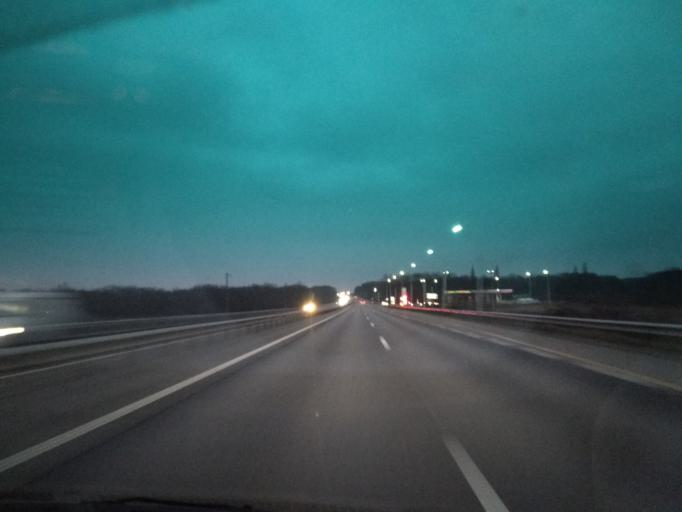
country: RU
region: Krasnodarskiy
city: Saratovskaya
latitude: 44.7943
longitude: 39.2329
